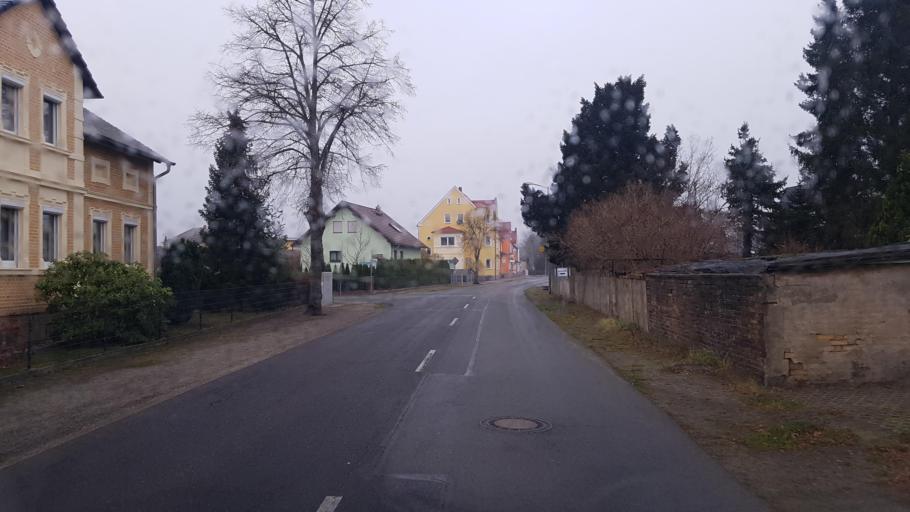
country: DE
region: Brandenburg
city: Lauchhammer
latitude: 51.4898
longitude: 13.7803
